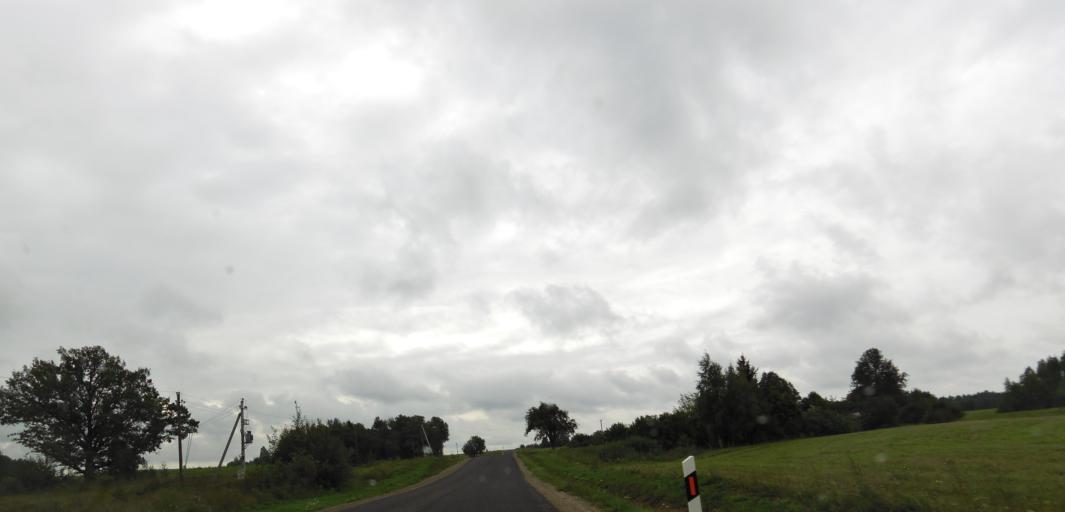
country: LT
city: Moletai
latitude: 55.2775
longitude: 25.3508
